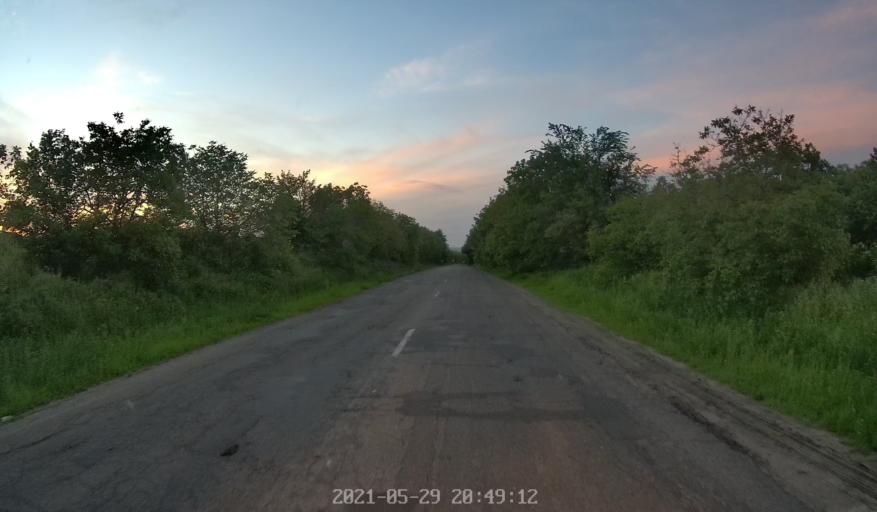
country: MD
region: Chisinau
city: Singera
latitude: 46.8603
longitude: 29.0316
